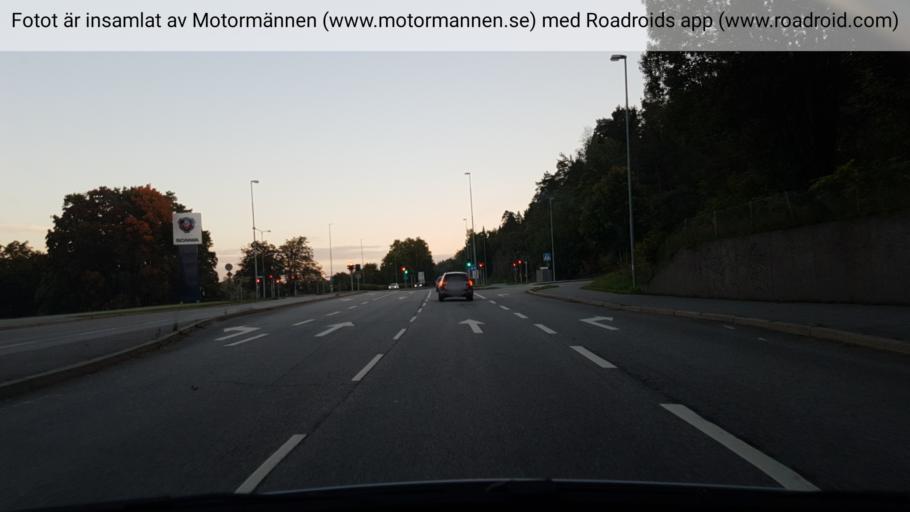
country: SE
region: Stockholm
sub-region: Sodertalje Kommun
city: Soedertaelje
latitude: 59.1834
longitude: 17.6308
